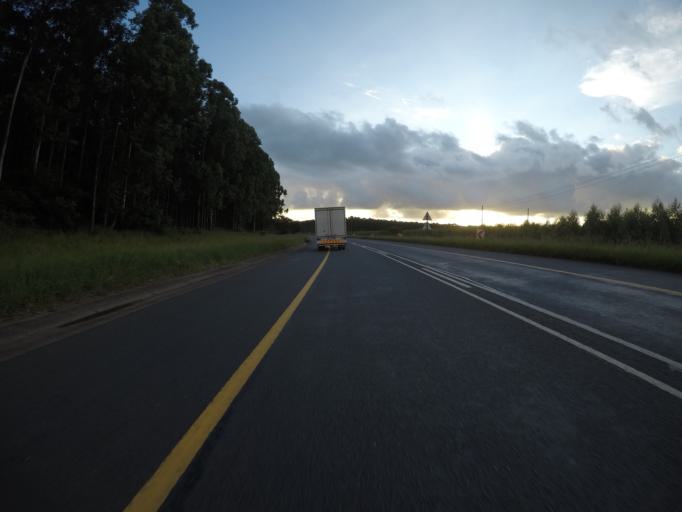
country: ZA
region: KwaZulu-Natal
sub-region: uThungulu District Municipality
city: KwaMbonambi
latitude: -28.5790
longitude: 32.1011
